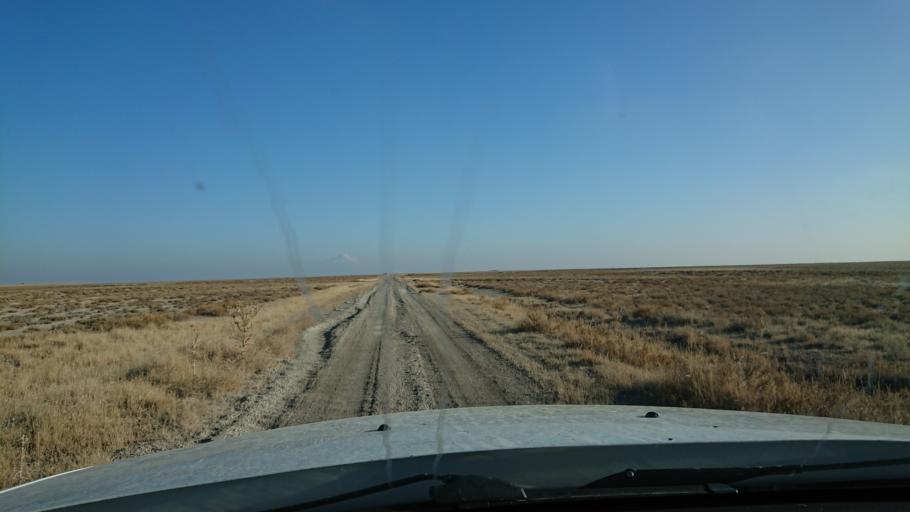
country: TR
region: Aksaray
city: Sultanhani
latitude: 38.4031
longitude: 33.5768
